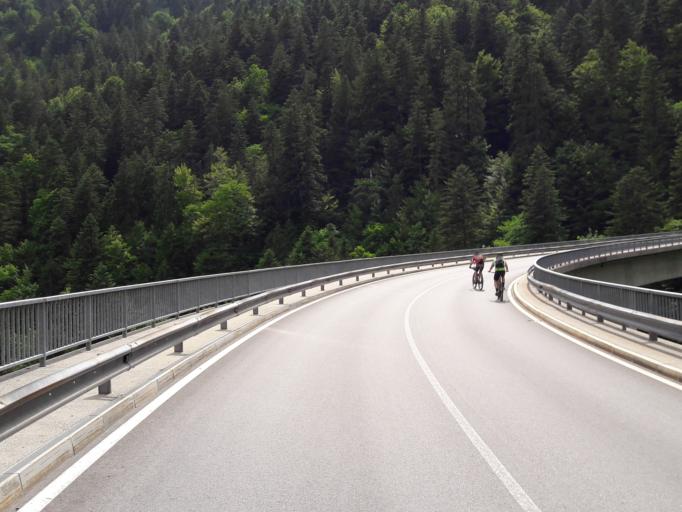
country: AT
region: Vorarlberg
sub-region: Politischer Bezirk Bludenz
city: Raggal
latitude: 47.2075
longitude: 9.8538
